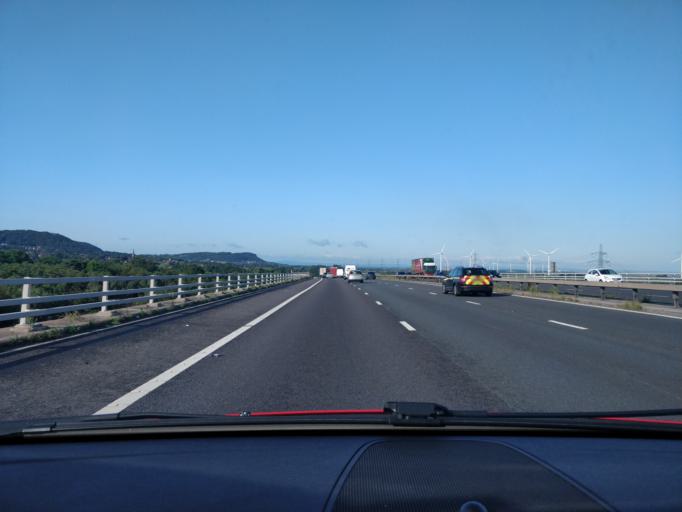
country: GB
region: England
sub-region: Borough of Halton
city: Halton
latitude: 53.3090
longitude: -2.7093
